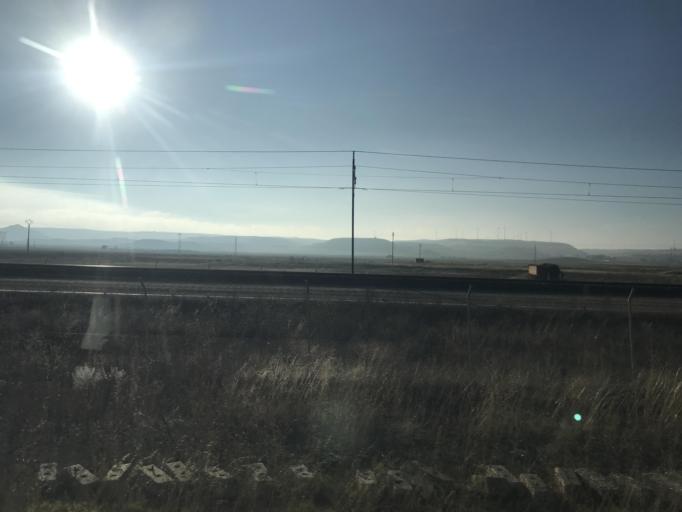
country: ES
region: Castille and Leon
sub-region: Provincia de Palencia
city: Quintana del Puente
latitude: 42.0714
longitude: -4.2120
